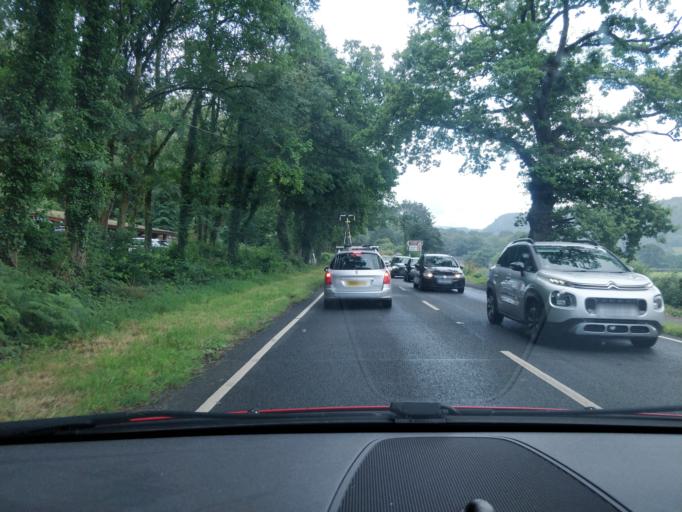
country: GB
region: Wales
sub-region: Conwy
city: Betws-y-Coed
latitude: 53.1014
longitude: -3.7874
